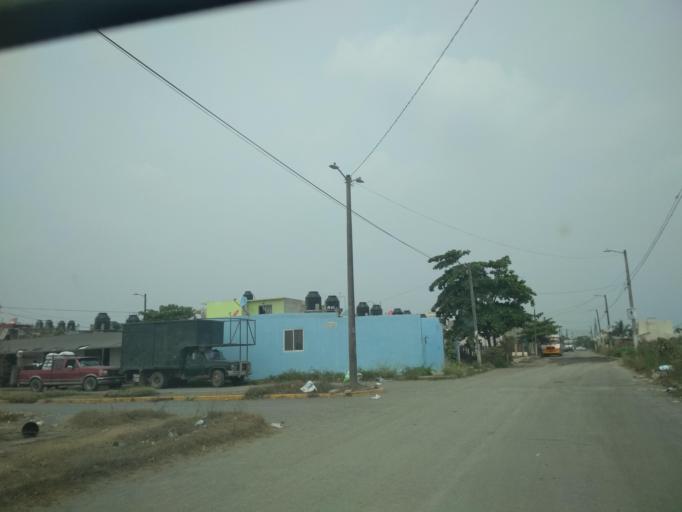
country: MX
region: Veracruz
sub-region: Veracruz
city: Arboledas
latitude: 19.2068
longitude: -96.2127
